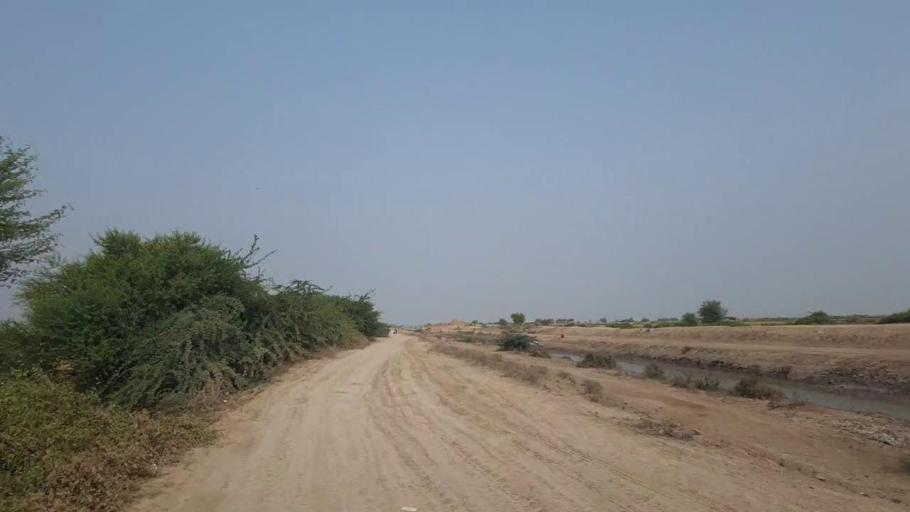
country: PK
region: Sindh
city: Badin
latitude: 24.7073
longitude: 68.7745
